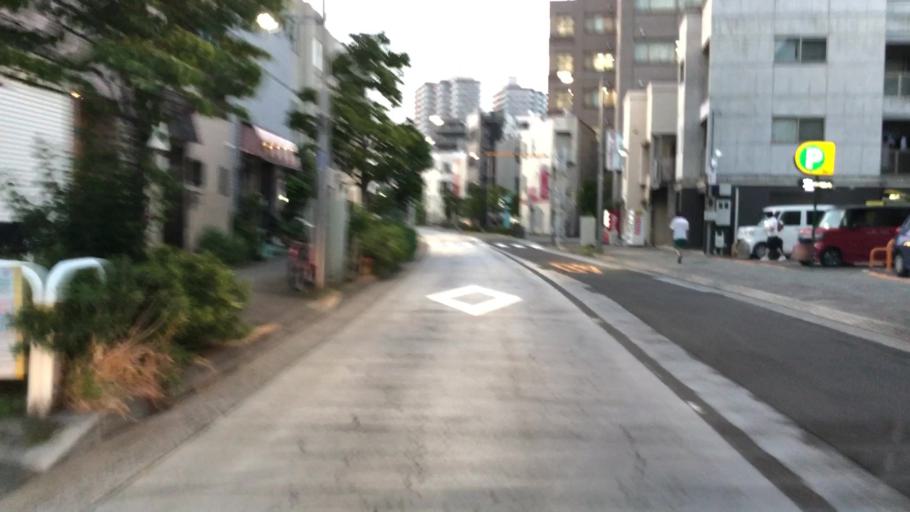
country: JP
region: Saitama
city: Soka
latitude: 35.7466
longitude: 139.7762
